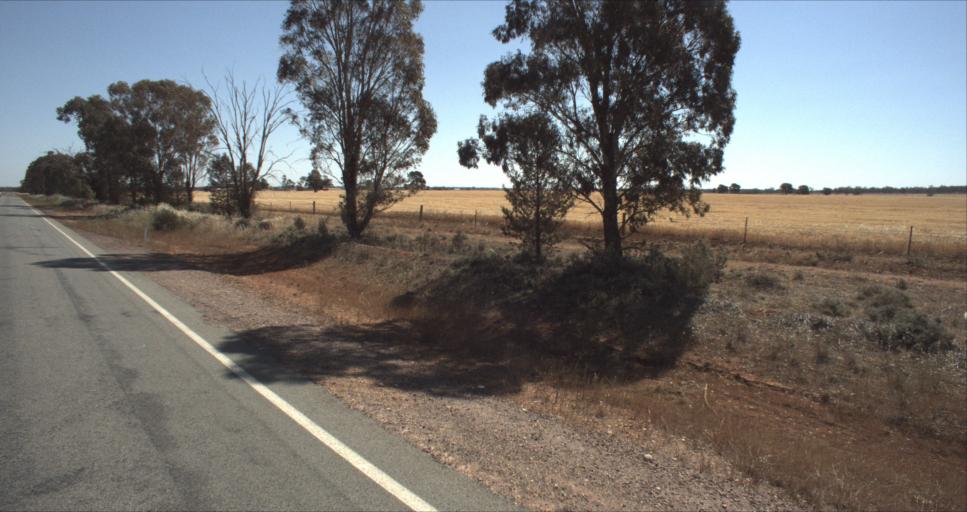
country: AU
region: New South Wales
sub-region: Leeton
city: Leeton
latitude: -34.4952
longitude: 146.4576
